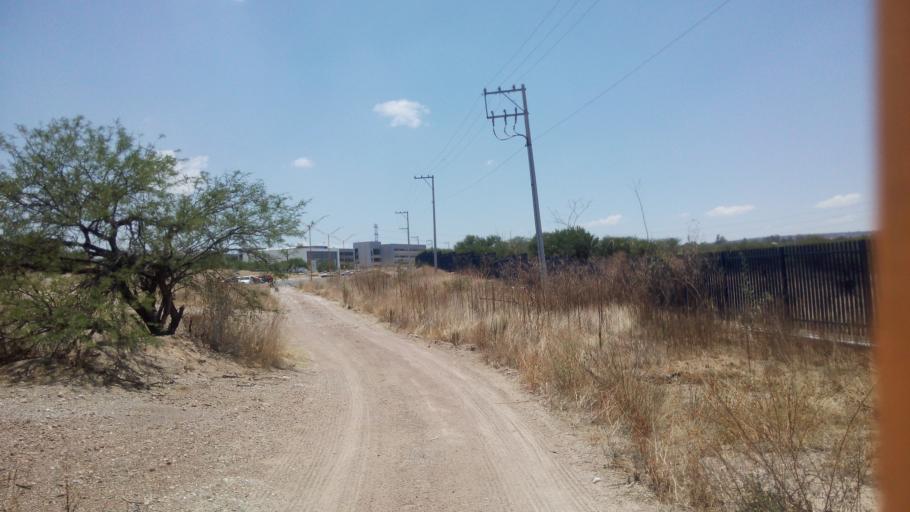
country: MX
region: Aguascalientes
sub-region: Aguascalientes
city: San Sebastian [Fraccionamiento]
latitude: 21.7911
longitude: -102.2935
